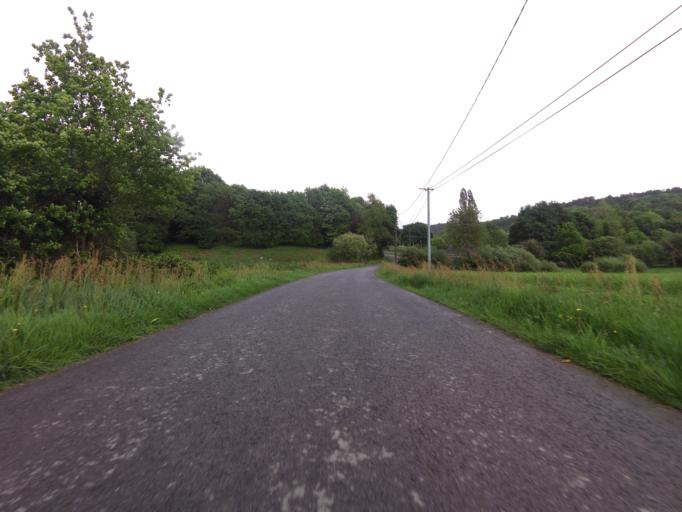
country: FR
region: Brittany
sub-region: Departement du Morbihan
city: Pluherlin
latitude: 47.7121
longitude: -2.3790
